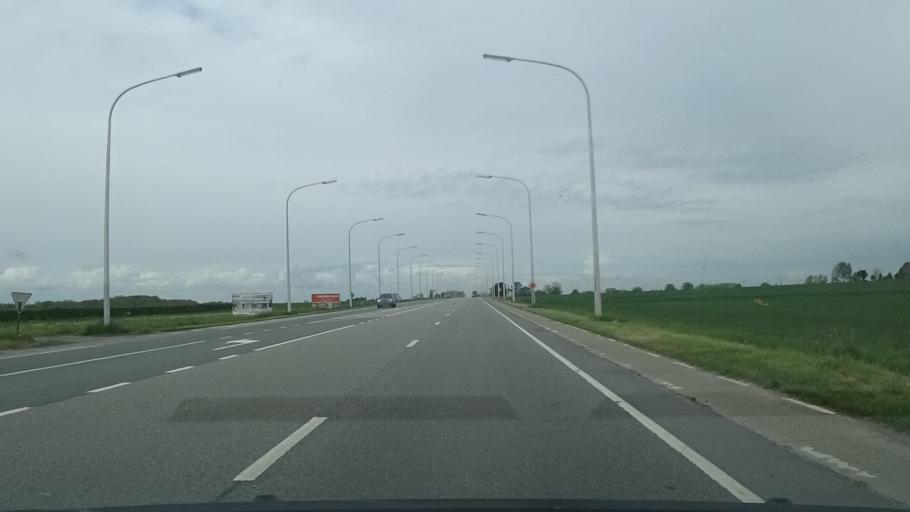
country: BE
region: Wallonia
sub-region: Province de Namur
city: Gembloux
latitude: 50.5205
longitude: 4.7621
